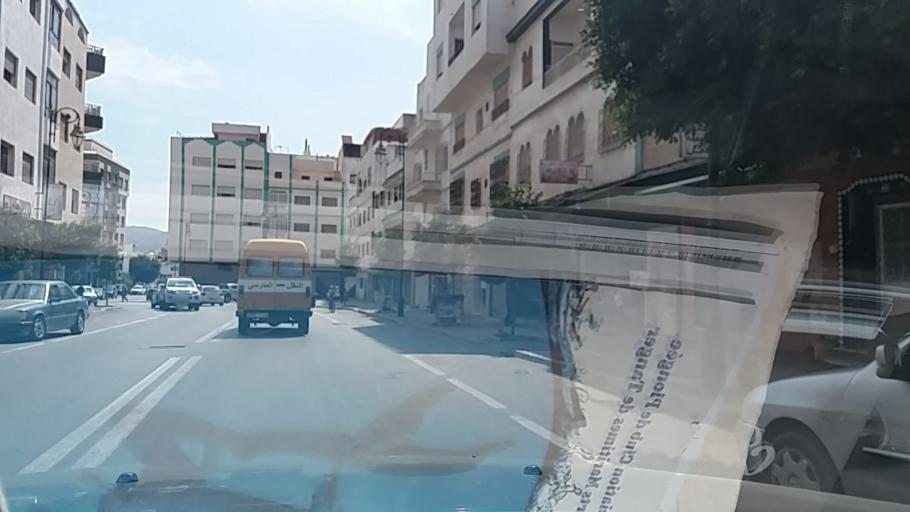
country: MA
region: Tanger-Tetouan
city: Tetouan
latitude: 35.5768
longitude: -5.3438
